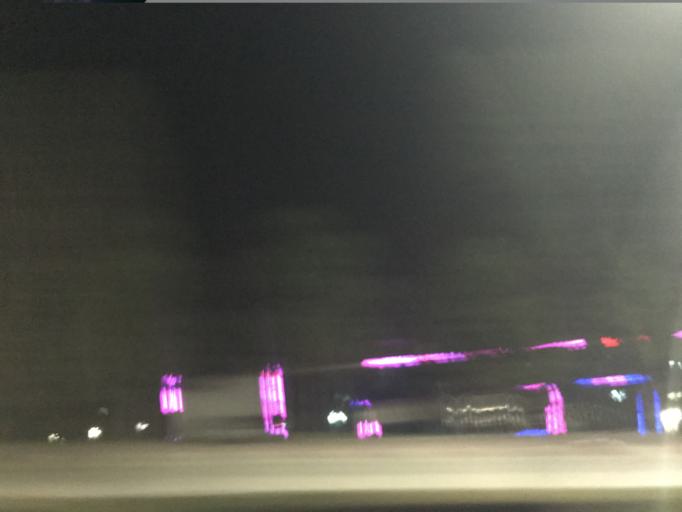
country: TR
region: Karabuk
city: Karabuk
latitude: 41.2083
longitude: 32.6569
